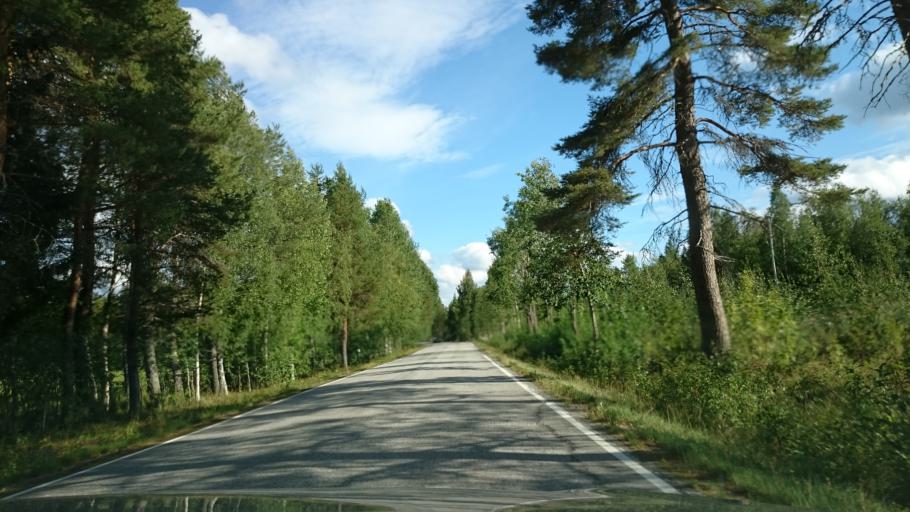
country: FI
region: Kainuu
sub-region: Kehys-Kainuu
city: Suomussalmi
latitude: 64.7591
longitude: 29.3876
